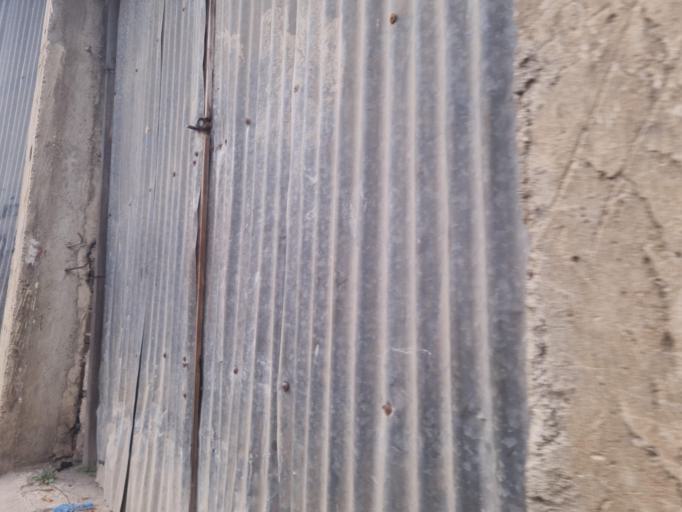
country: GT
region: Quetzaltenango
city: Quetzaltenango
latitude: 14.8308
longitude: -91.5307
